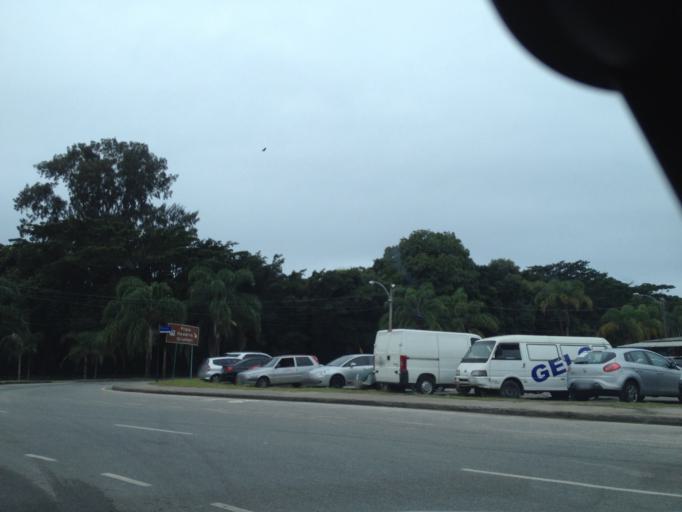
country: BR
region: Rio de Janeiro
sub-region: Nilopolis
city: Nilopolis
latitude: -23.0187
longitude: -43.4513
